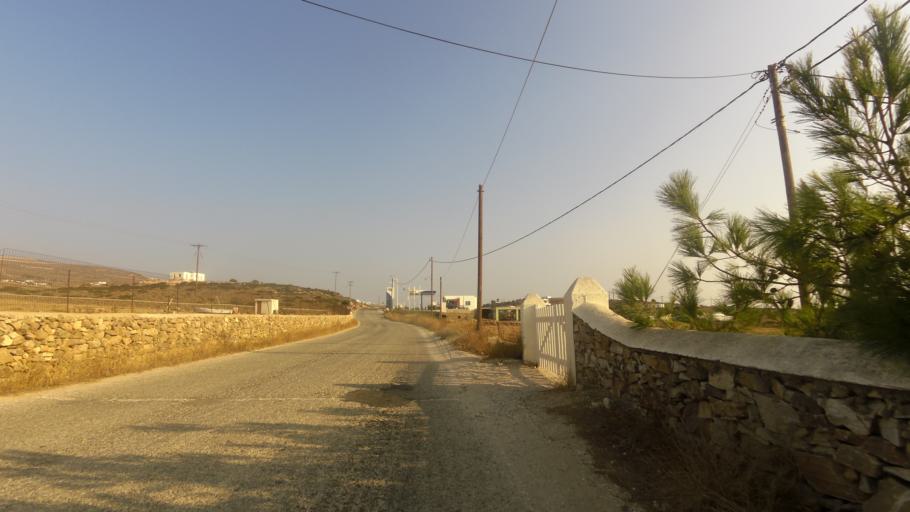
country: GR
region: South Aegean
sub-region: Nomos Kykladon
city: Antiparos
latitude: 37.0276
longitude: 25.0763
